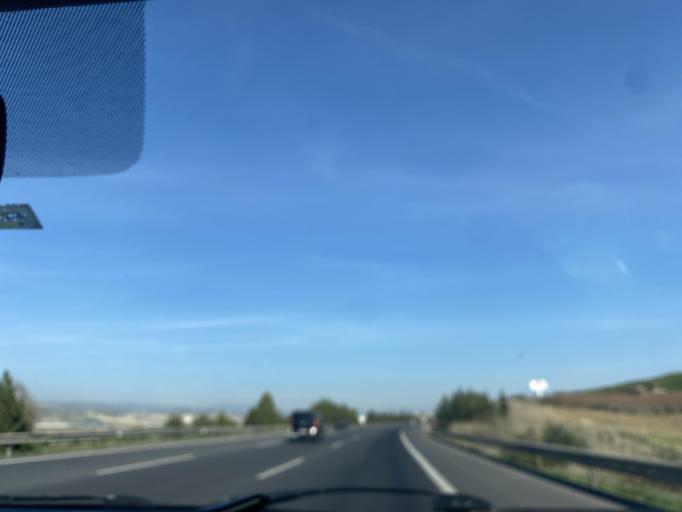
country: TR
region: Mersin
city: Tarsus
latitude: 36.9932
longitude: 34.9288
